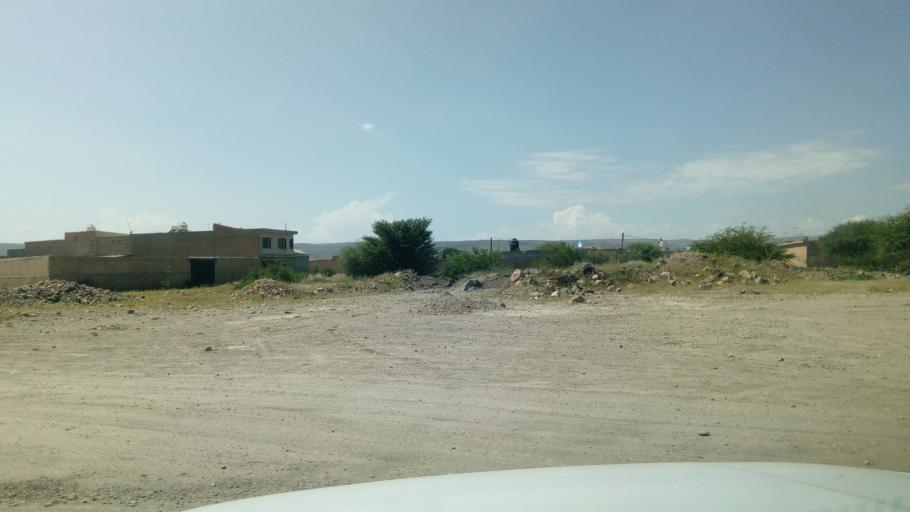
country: MX
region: Durango
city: Victoria de Durango
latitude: 23.9885
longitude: -104.6843
